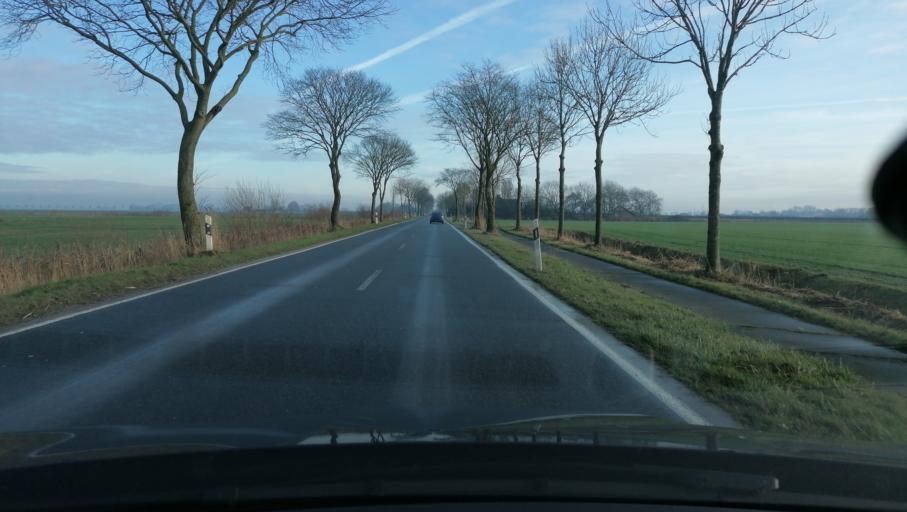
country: DE
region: Schleswig-Holstein
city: Wohrden
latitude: 54.1215
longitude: 8.9953
